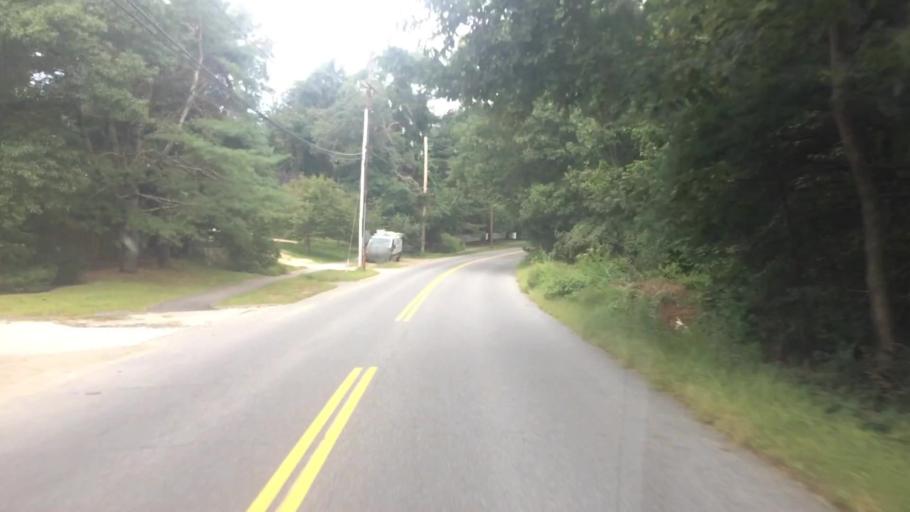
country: US
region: Massachusetts
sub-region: Middlesex County
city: West Concord
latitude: 42.4608
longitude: -71.4173
